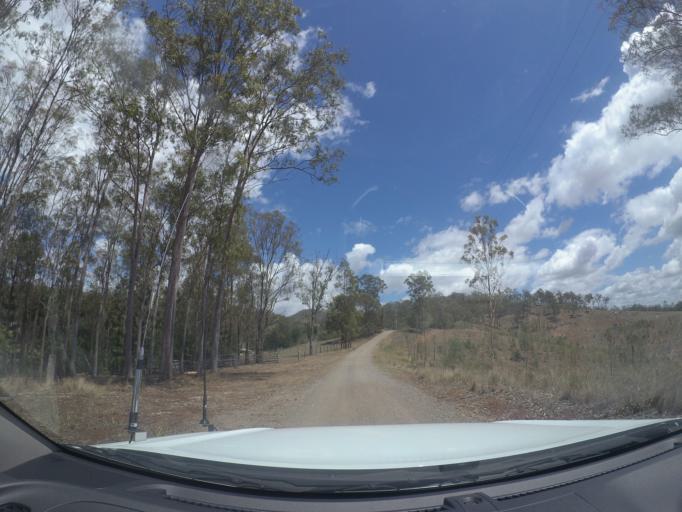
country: AU
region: Queensland
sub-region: Logan
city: Cedar Vale
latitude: -27.9150
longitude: 153.0523
